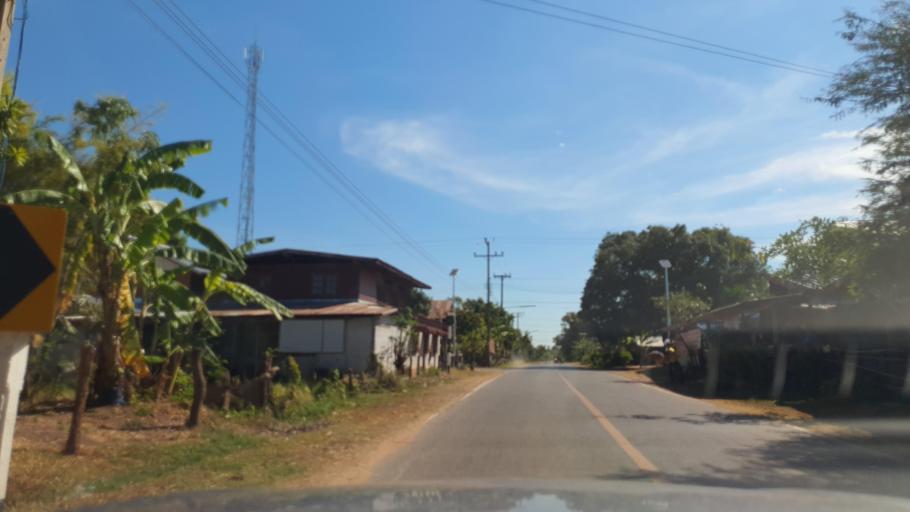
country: TH
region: Kalasin
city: Khao Wong
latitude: 16.7156
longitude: 104.1144
